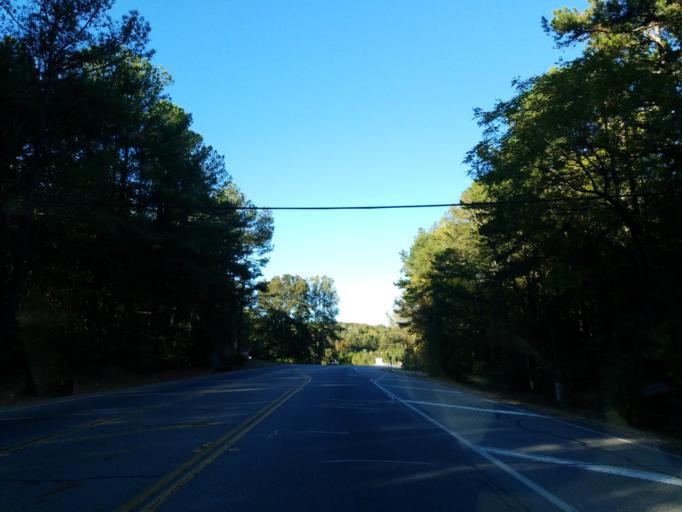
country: US
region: Georgia
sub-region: Cherokee County
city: Ball Ground
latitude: 34.3604
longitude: -84.3779
